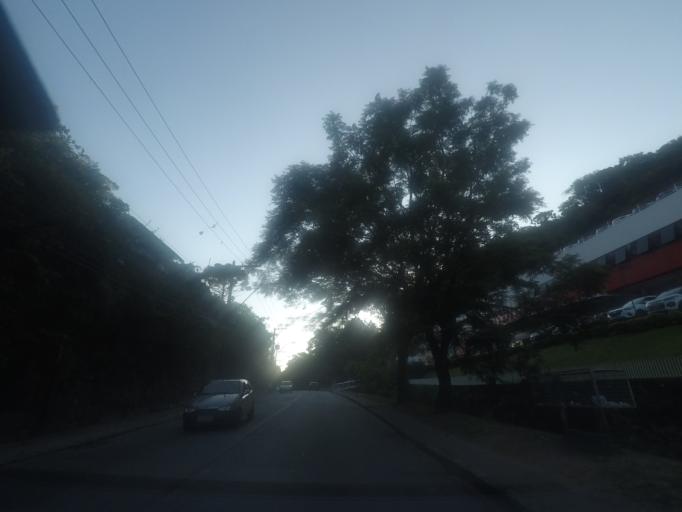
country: BR
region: Rio de Janeiro
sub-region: Petropolis
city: Petropolis
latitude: -22.5305
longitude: -43.1982
